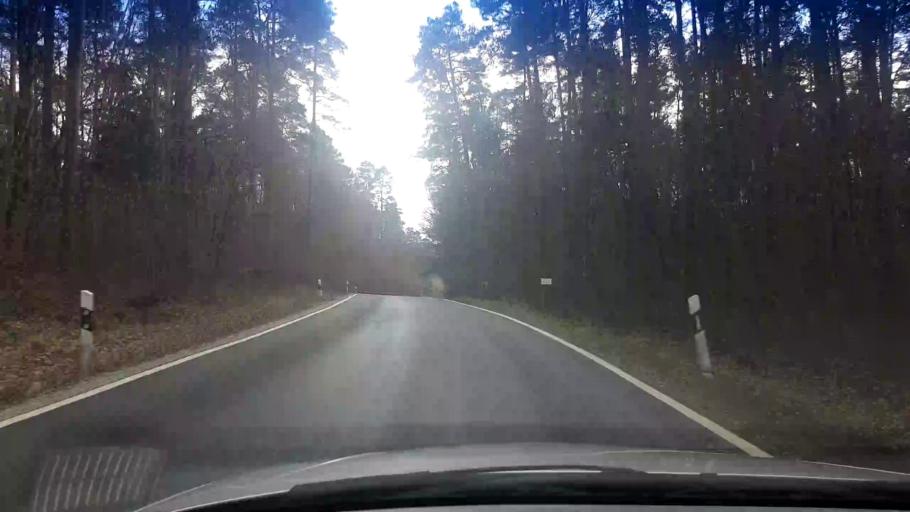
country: DE
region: Bavaria
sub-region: Upper Franconia
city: Burgebrach
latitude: 49.8105
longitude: 10.7843
